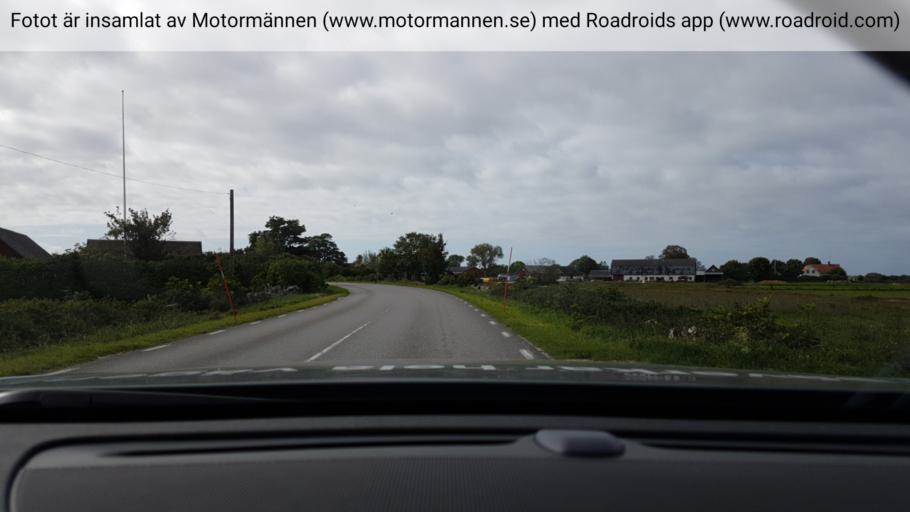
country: SE
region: Gotland
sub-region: Gotland
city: Hemse
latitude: 56.9681
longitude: 18.2303
